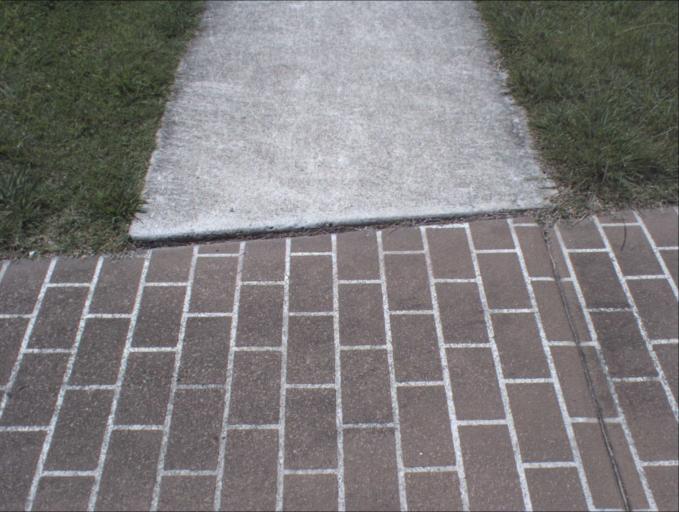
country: AU
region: Queensland
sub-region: Logan
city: Woodridge
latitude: -27.6588
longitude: 153.0754
